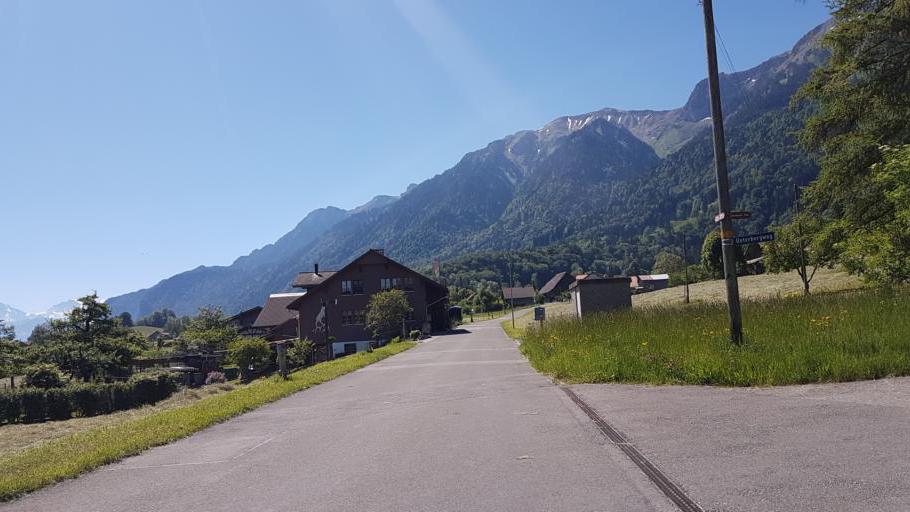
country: CH
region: Bern
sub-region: Thun District
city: Blumenstein
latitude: 46.7351
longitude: 7.5116
